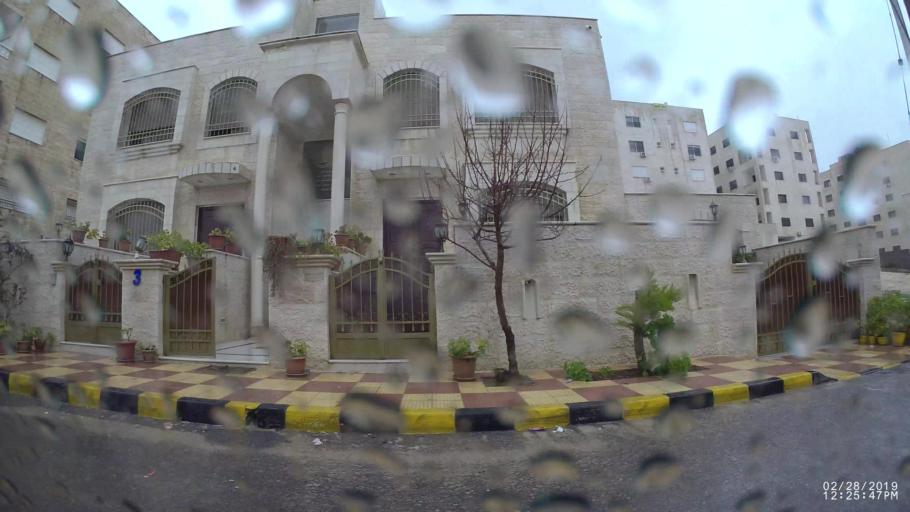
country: JO
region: Amman
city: Al Jubayhah
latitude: 32.0263
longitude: 35.8903
